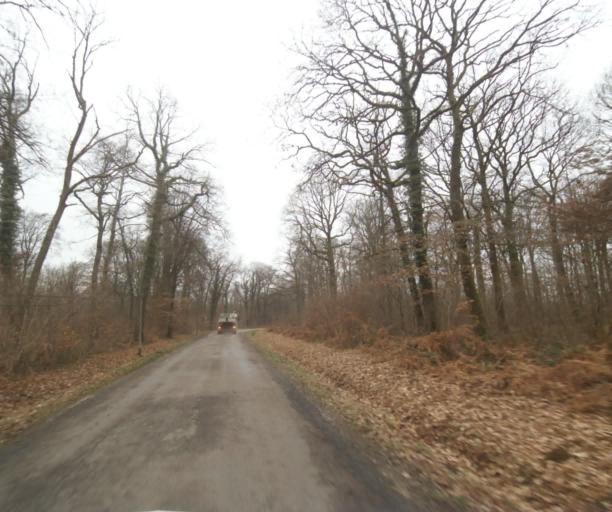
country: FR
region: Champagne-Ardenne
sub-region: Departement de la Haute-Marne
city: Wassy
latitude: 48.5224
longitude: 4.9749
